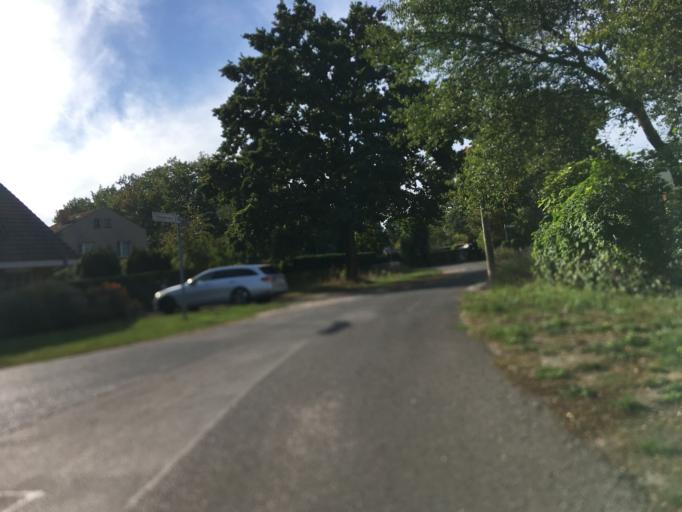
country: DE
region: Berlin
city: Mahlsdorf
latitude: 52.5130
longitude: 13.6265
